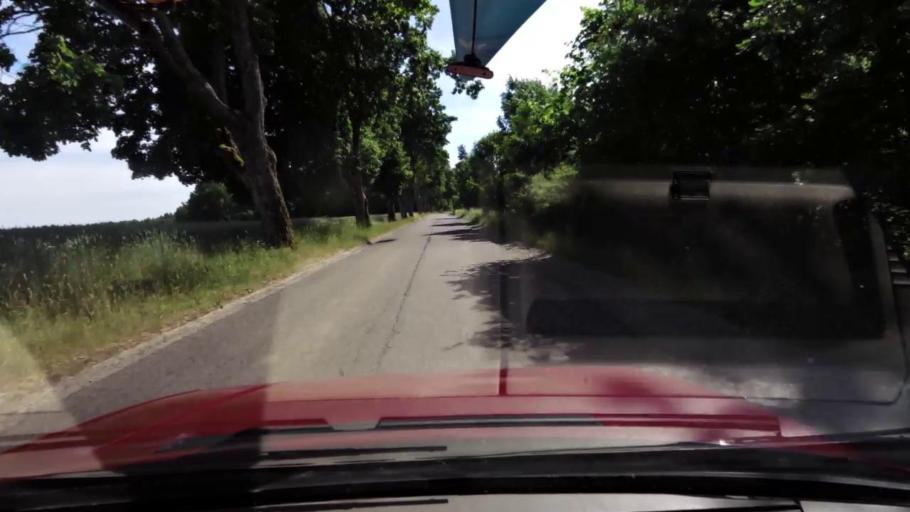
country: PL
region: Pomeranian Voivodeship
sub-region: Powiat slupski
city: Kobylnica
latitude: 54.3450
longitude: 16.9655
